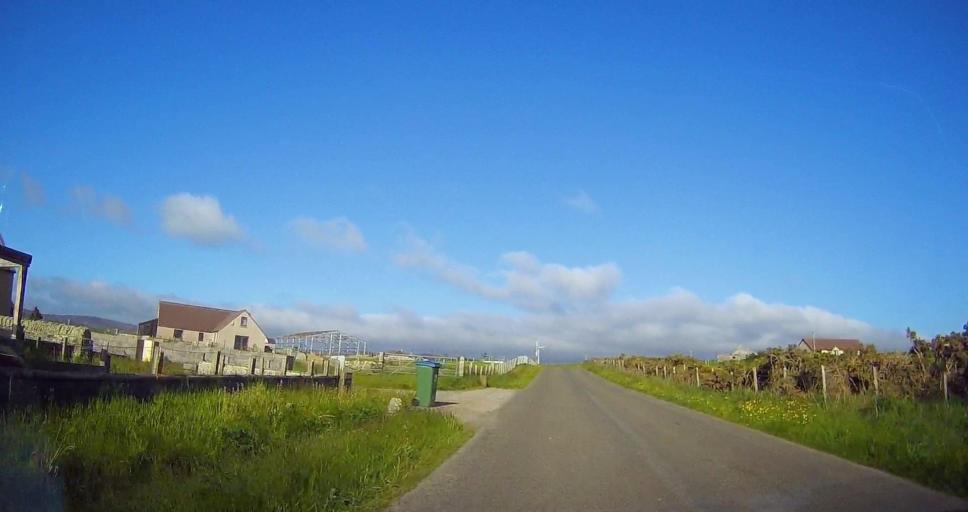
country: GB
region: Scotland
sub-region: Orkney Islands
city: Stromness
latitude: 59.0738
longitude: -3.2135
